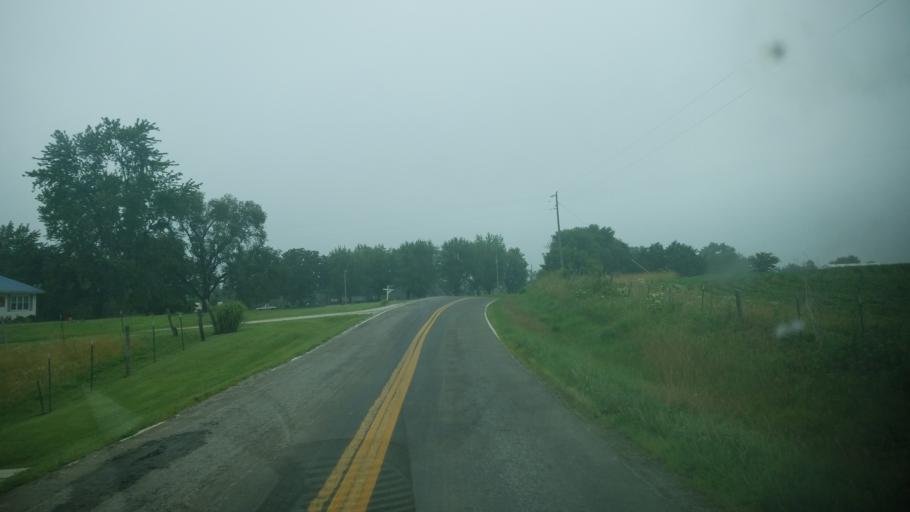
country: US
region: Missouri
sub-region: Audrain County
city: Vandalia
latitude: 39.2786
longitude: -91.3468
